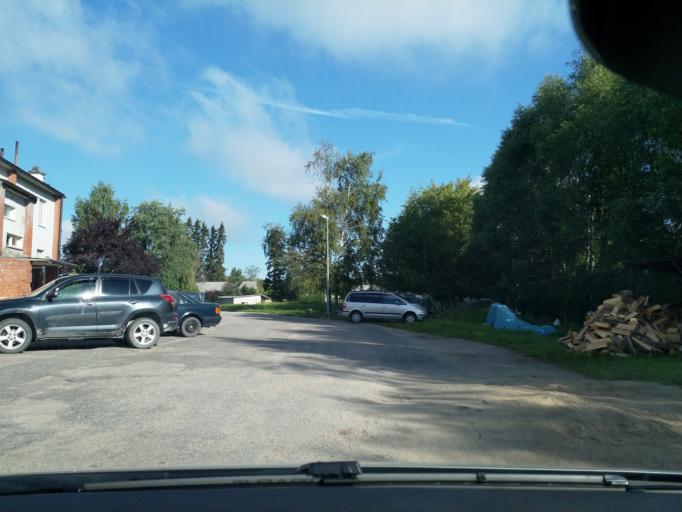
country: LV
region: Kuldigas Rajons
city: Kuldiga
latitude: 56.9664
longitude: 22.0063
